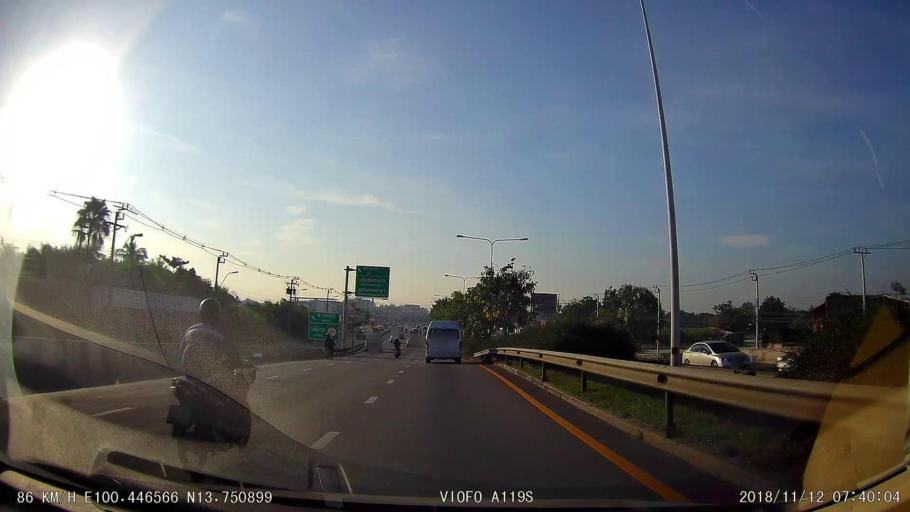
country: TH
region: Bangkok
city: Taling Chan
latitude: 13.7501
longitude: 100.4468
